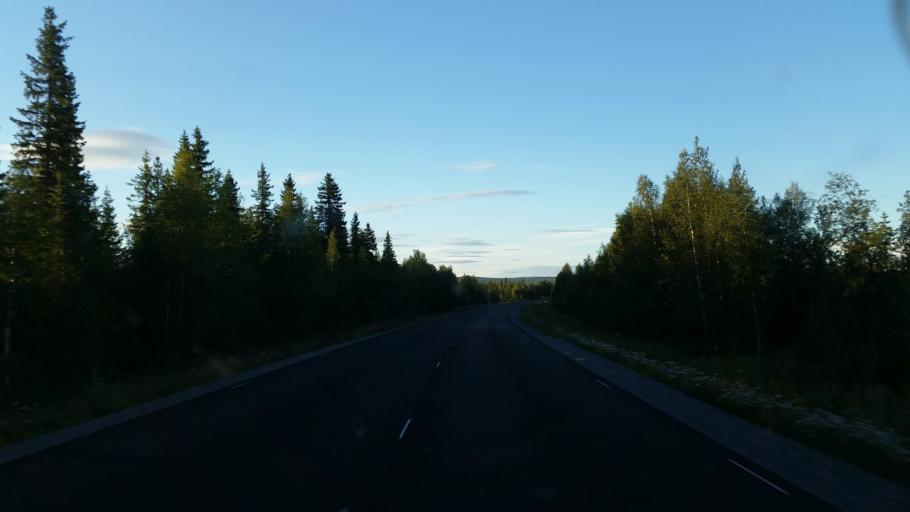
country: SE
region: Vaesterbotten
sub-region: Vilhelmina Kommun
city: Vilhelmina
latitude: 64.7845
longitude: 16.7692
